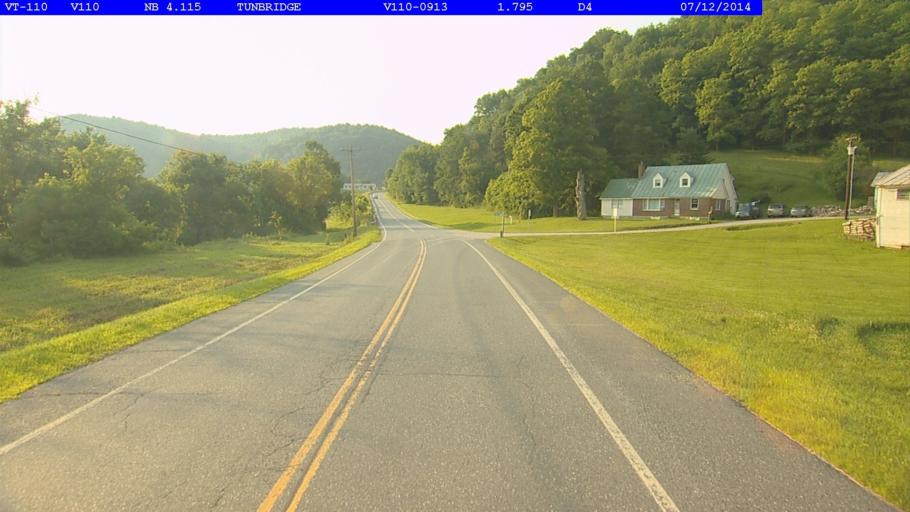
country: US
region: Vermont
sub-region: Orange County
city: Chelsea
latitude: 43.8766
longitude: -72.4993
